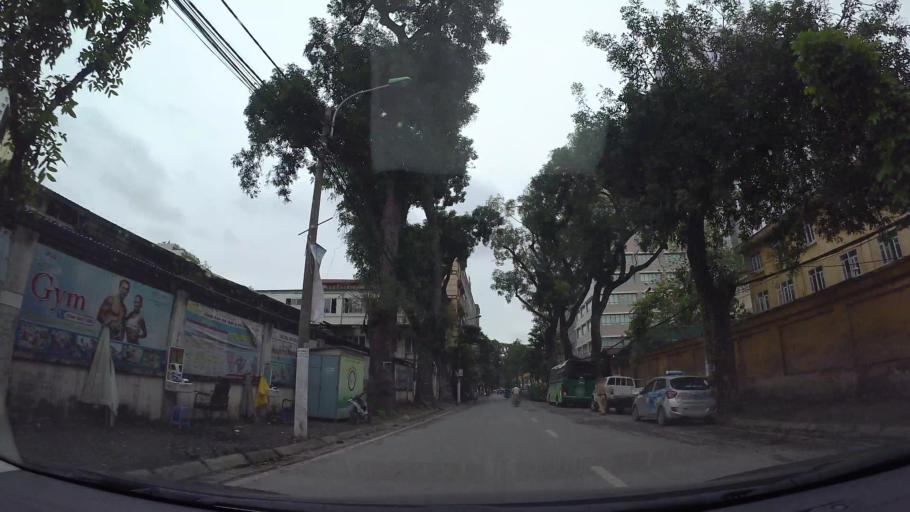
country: VN
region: Ha Noi
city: Hai BaTrung
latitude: 21.0153
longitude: 105.8596
